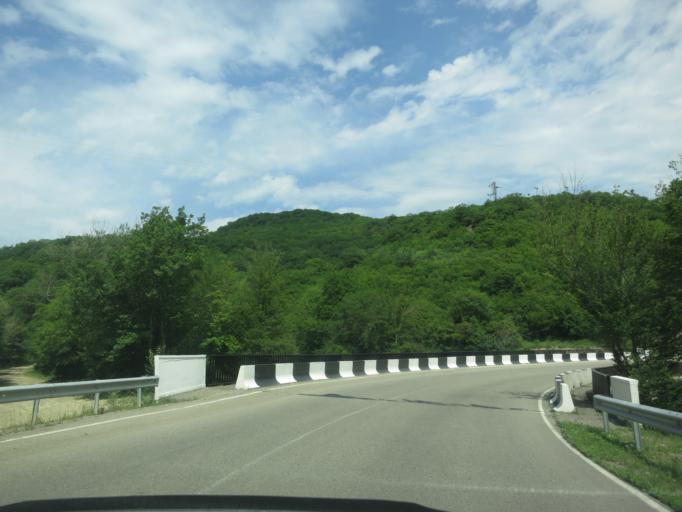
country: GE
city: Didi Lilo
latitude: 41.8197
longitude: 45.1375
